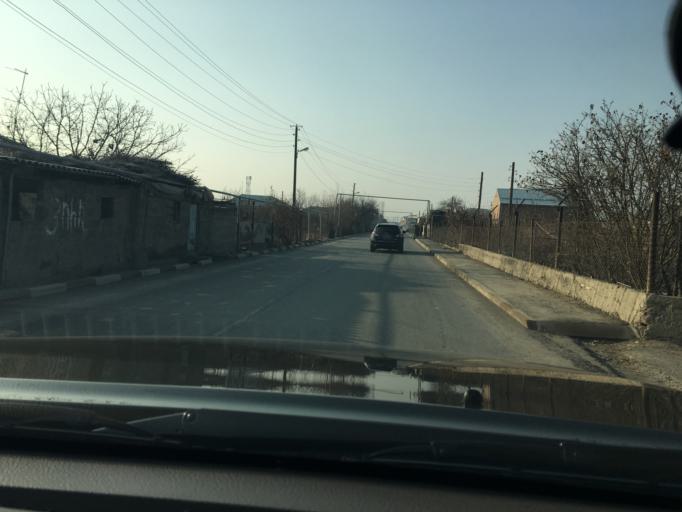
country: AM
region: Armavir
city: Janfida
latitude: 40.0514
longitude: 44.0328
